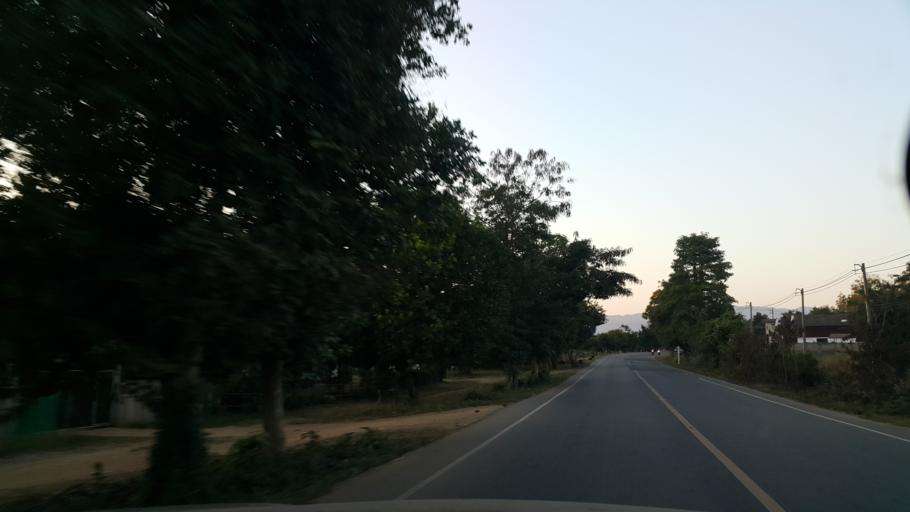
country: TH
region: Phrae
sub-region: Amphoe Wang Chin
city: Wang Chin
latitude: 17.8461
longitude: 99.6292
